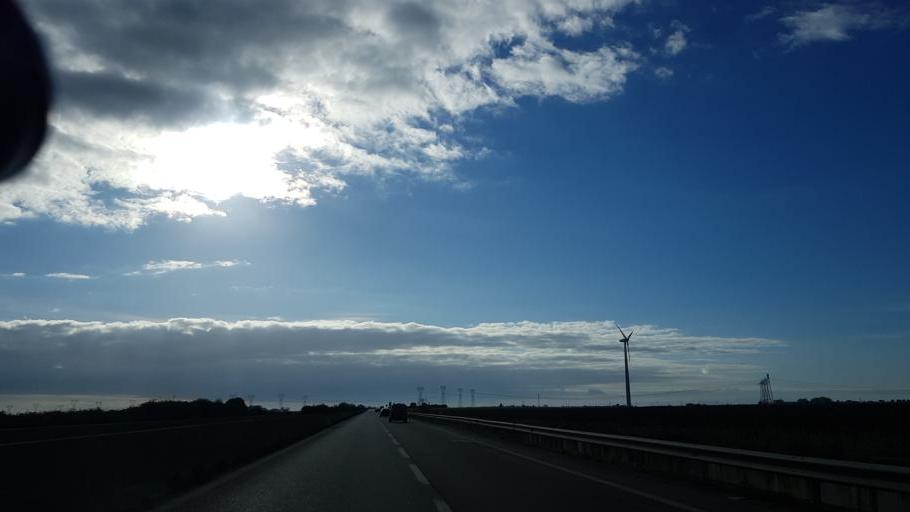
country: IT
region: Apulia
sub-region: Provincia di Brindisi
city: Tuturano
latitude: 40.5713
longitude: 17.9835
